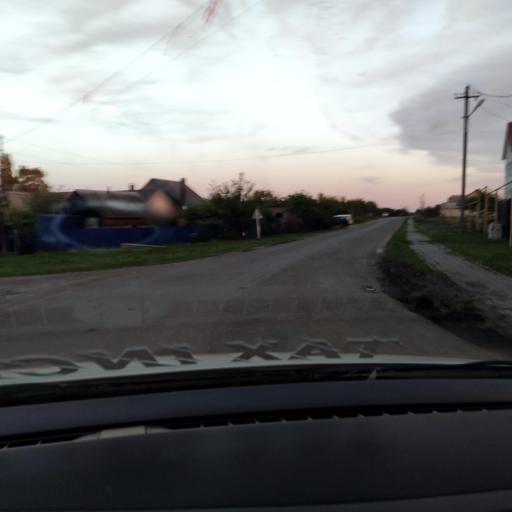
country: RU
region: Voronezj
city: Maslovka
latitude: 51.4551
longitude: 39.2404
